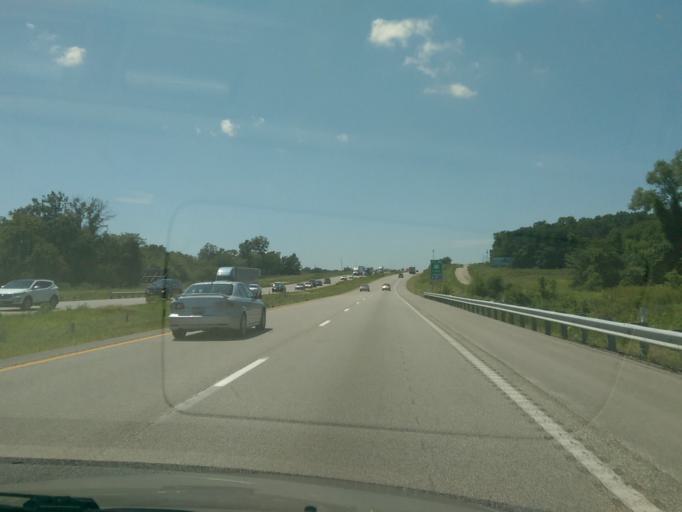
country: US
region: Missouri
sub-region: Saline County
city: Marshall
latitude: 38.9702
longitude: -93.2472
